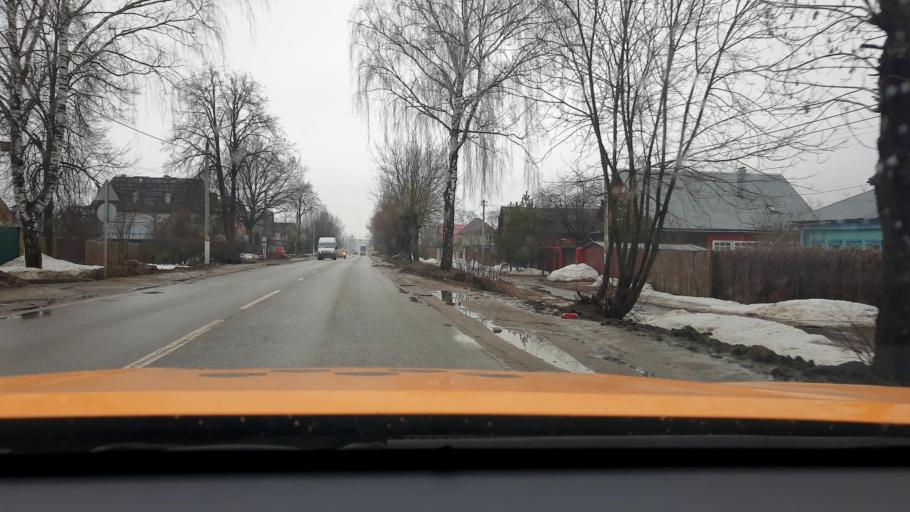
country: RU
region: Moskovskaya
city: Noginsk
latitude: 55.8933
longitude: 38.4485
